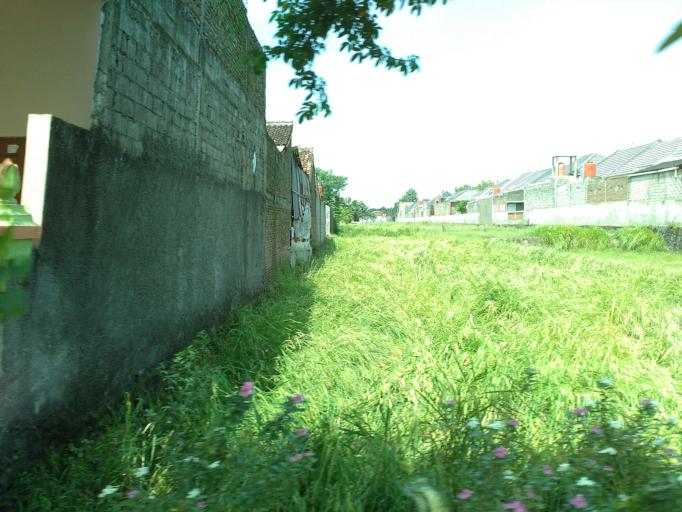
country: ID
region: Central Java
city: Kebonarun
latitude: -7.7165
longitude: 110.5782
